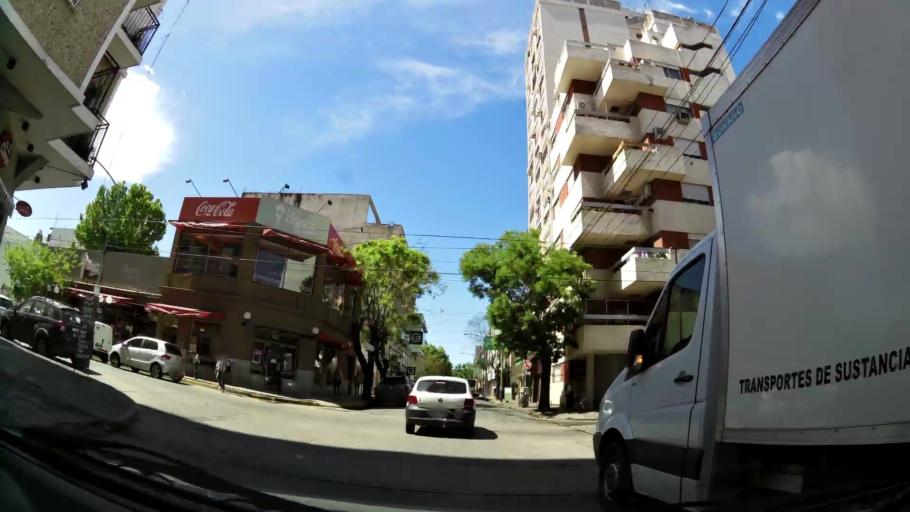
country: AR
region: Buenos Aires
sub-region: Partido de Quilmes
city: Quilmes
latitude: -34.7239
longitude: -58.2572
